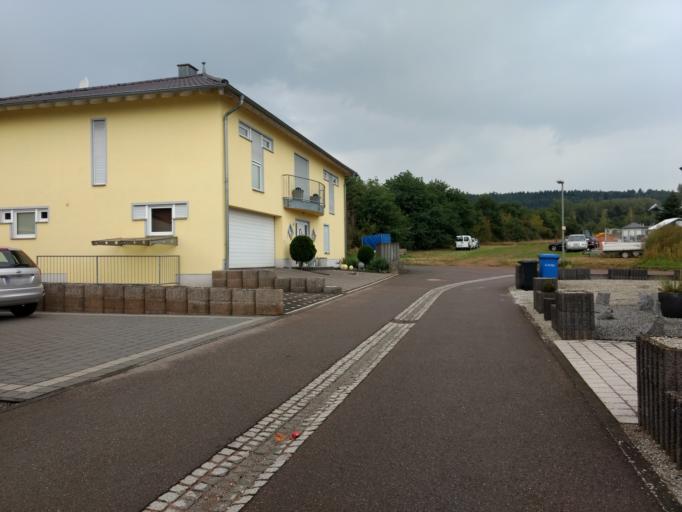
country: DE
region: Saarland
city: Nalbach
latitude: 49.3912
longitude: 6.7978
